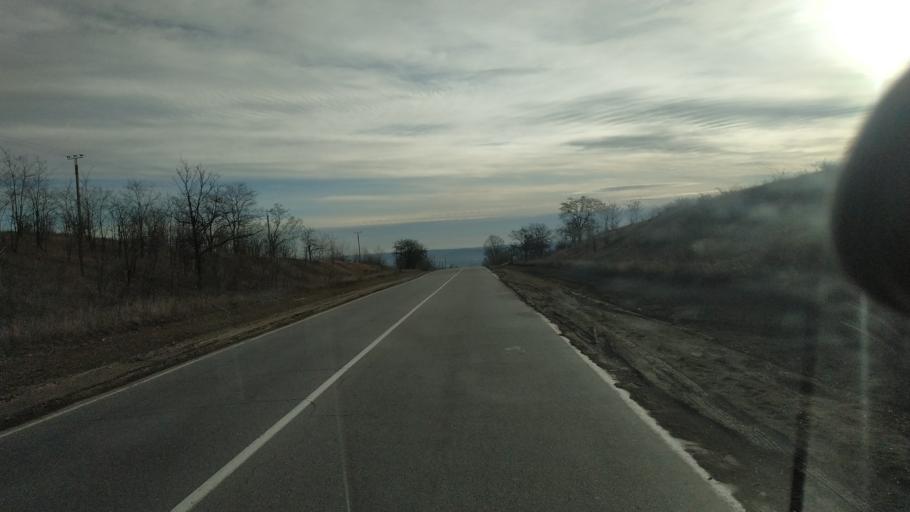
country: MD
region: Chisinau
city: Vadul lui Voda
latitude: 47.0884
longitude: 29.0515
